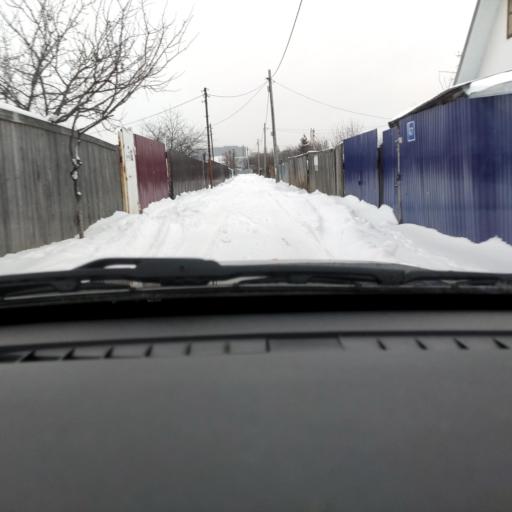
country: RU
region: Samara
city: Tol'yatti
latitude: 53.5399
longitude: 49.4342
